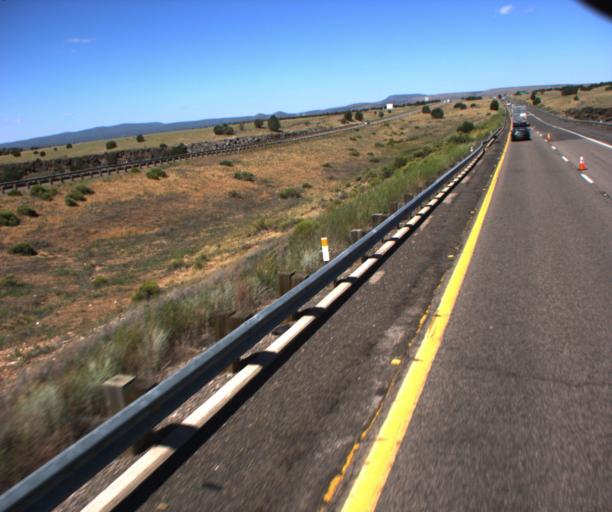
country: US
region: Arizona
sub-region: Mohave County
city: Peach Springs
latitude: 35.3223
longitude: -112.9055
